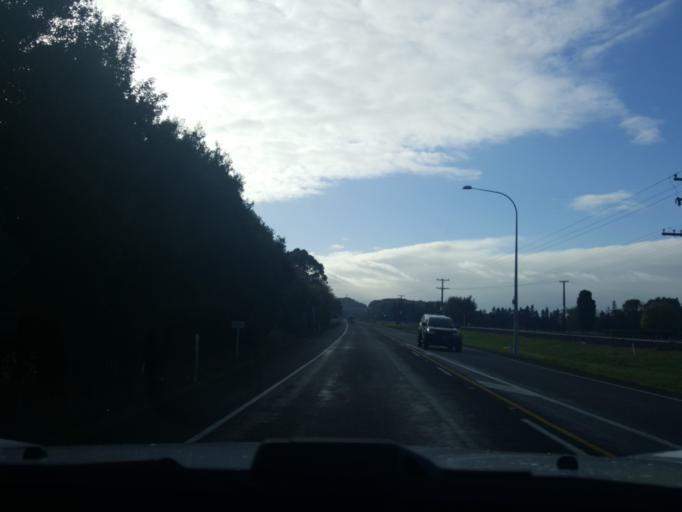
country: NZ
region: Waikato
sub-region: Waipa District
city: Cambridge
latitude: -37.6681
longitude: 175.4850
